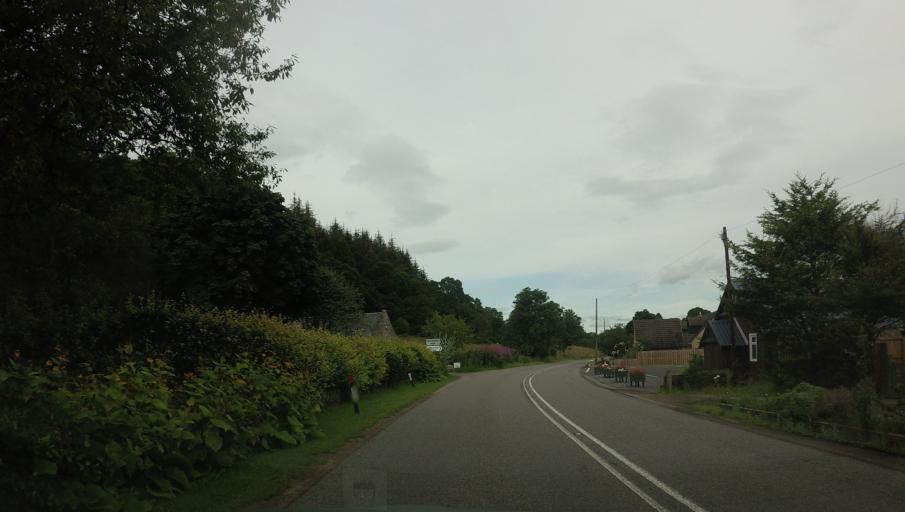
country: GB
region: Scotland
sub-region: Aberdeenshire
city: Torphins
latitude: 57.0640
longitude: -2.5720
